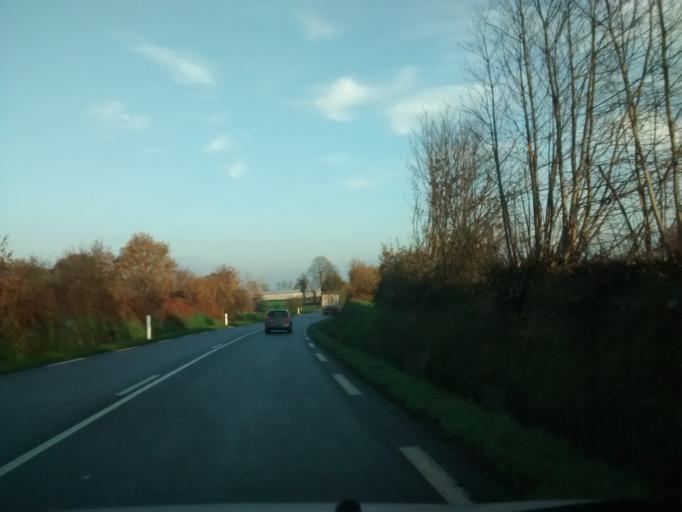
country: FR
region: Brittany
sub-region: Departement d'Ille-et-Vilaine
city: Tremblay
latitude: 48.4400
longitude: -1.4781
